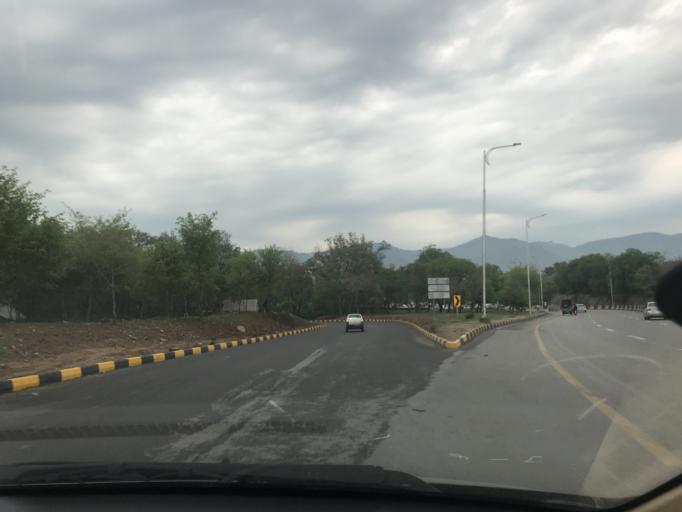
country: PK
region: Islamabad
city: Islamabad
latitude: 33.7115
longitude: 73.1035
